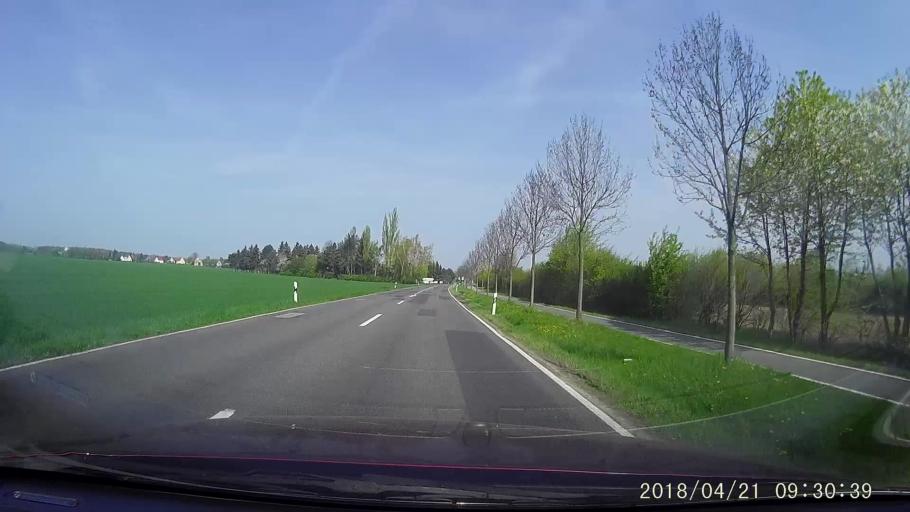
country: DE
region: Saxony
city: Bautzen
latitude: 51.2027
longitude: 14.4043
